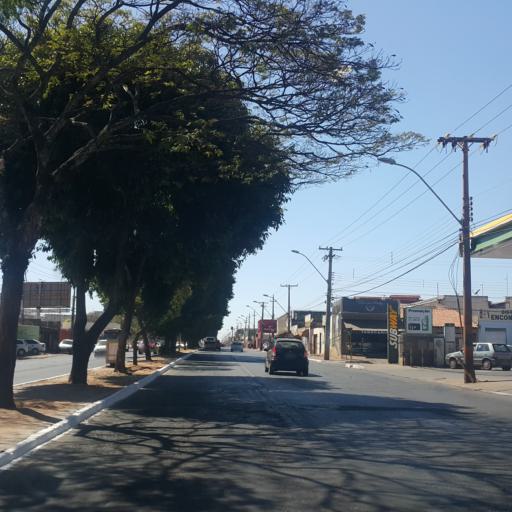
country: BR
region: Federal District
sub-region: Brasilia
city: Brasilia
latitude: -15.8030
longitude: -48.0671
